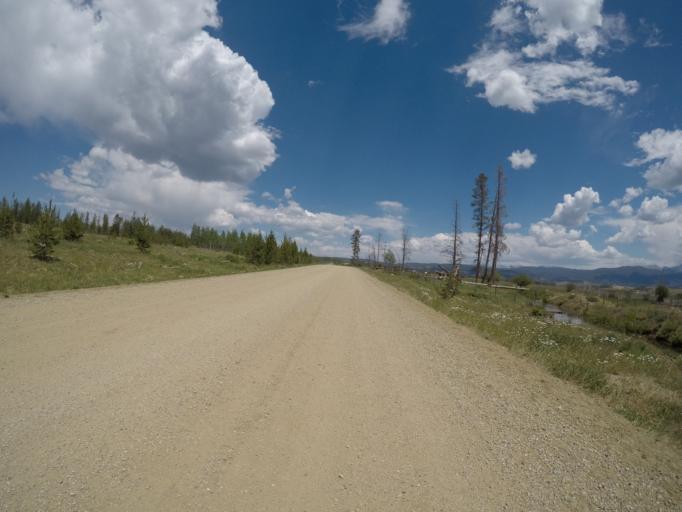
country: US
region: Colorado
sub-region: Grand County
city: Fraser
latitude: 39.9531
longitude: -105.8688
